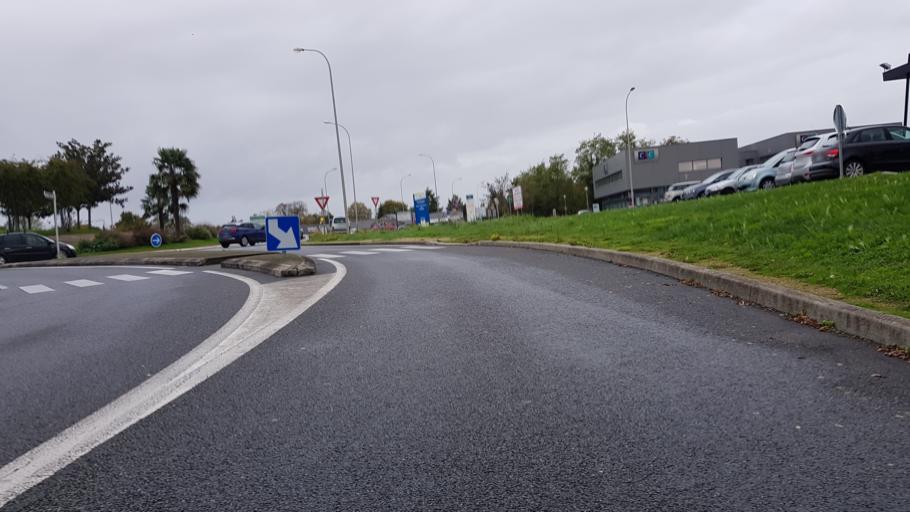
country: FR
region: Poitou-Charentes
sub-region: Departement de la Vienne
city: Jaunay-Clan
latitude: 46.6717
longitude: 0.3764
